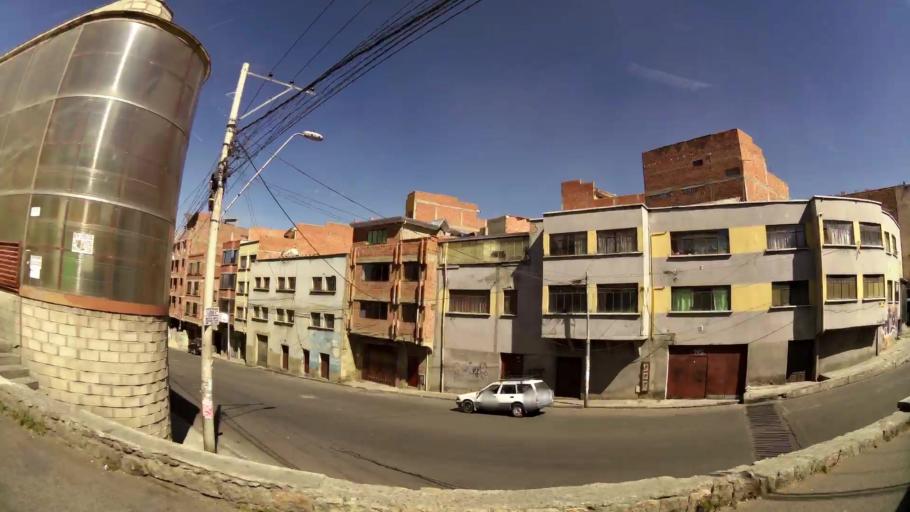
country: BO
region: La Paz
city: La Paz
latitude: -16.4975
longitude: -68.1494
